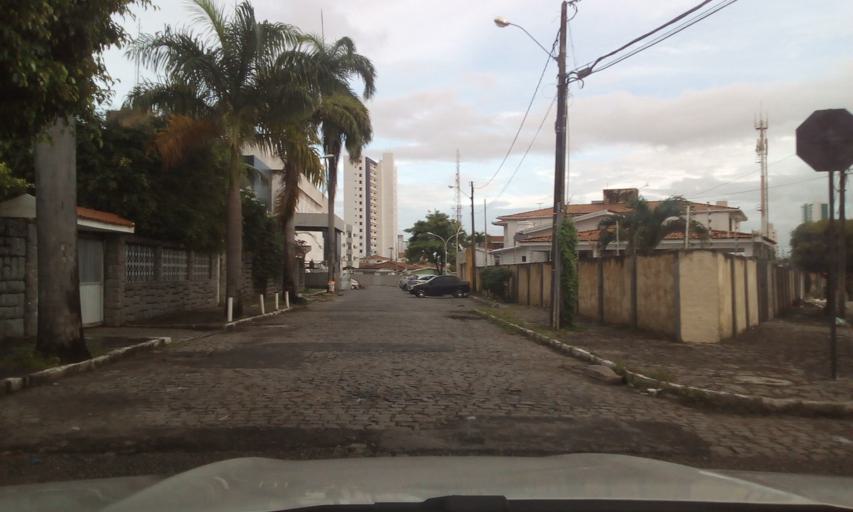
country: BR
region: Paraiba
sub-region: Joao Pessoa
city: Joao Pessoa
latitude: -7.1104
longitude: -34.8565
